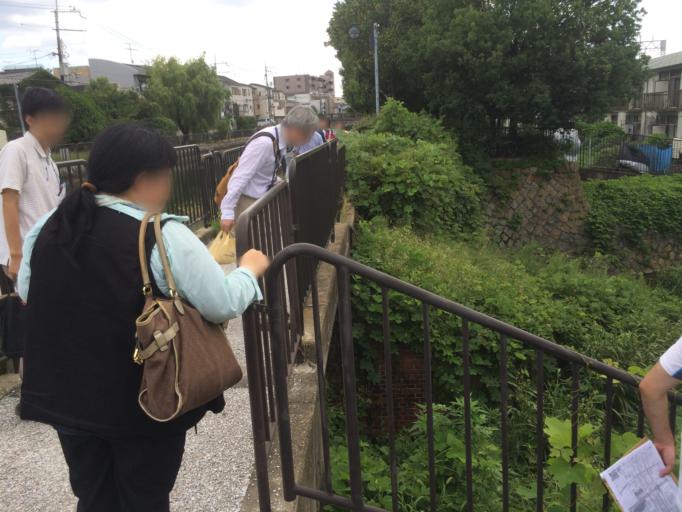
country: JP
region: Kyoto
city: Muko
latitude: 34.9533
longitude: 135.7702
